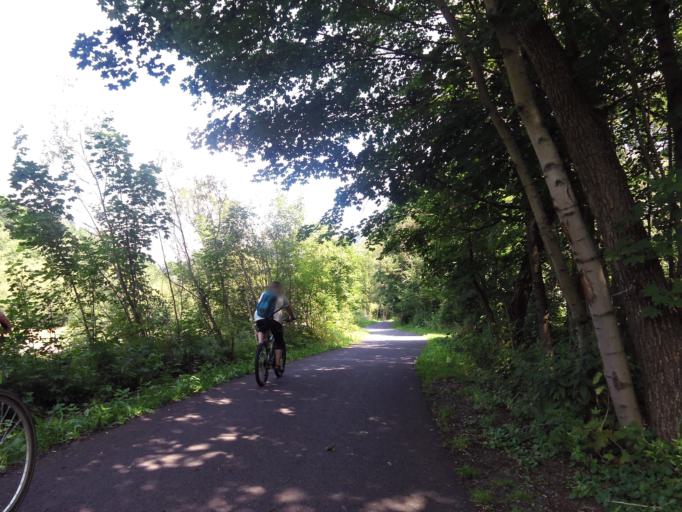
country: PL
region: Silesian Voivodeship
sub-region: Powiat zywiecki
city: Rajcza
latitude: 49.5110
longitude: 19.1142
